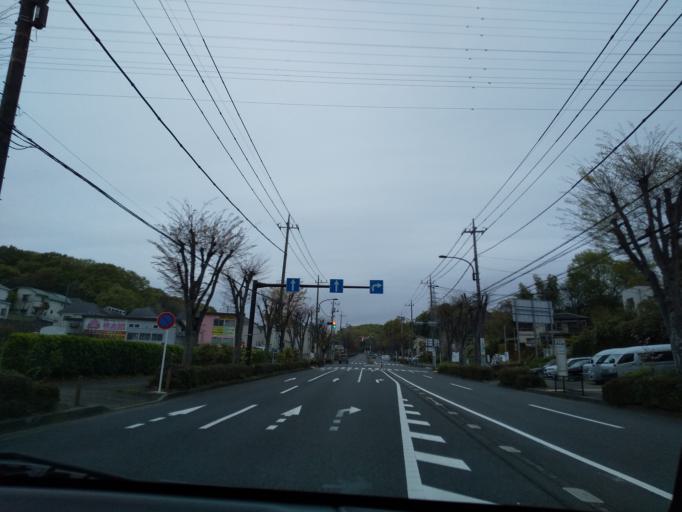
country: JP
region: Tokyo
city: Hino
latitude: 35.6312
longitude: 139.3725
